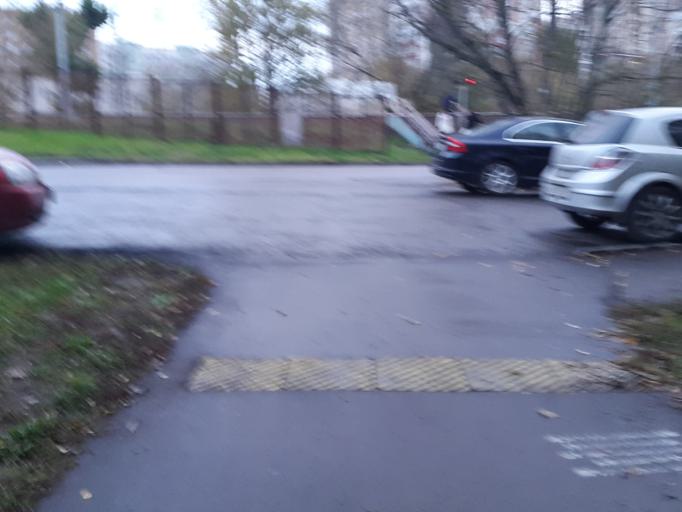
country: RU
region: Moscow
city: Pokrovskoye-Streshnevo
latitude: 55.8117
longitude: 37.4548
